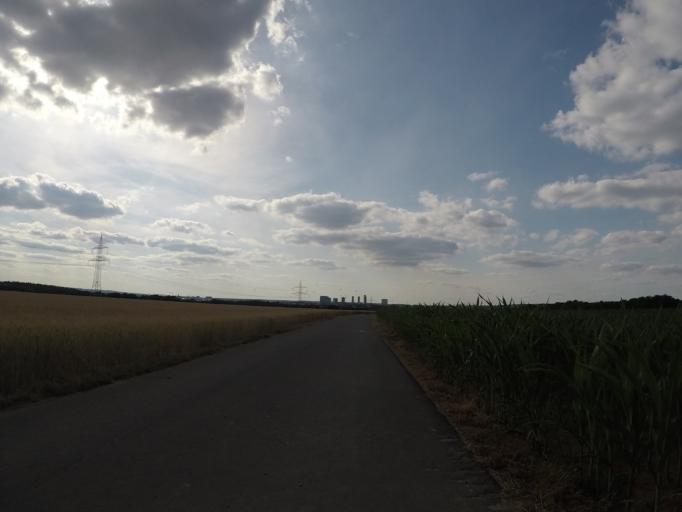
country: LU
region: Luxembourg
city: Itzig
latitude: 49.6001
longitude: 6.1814
